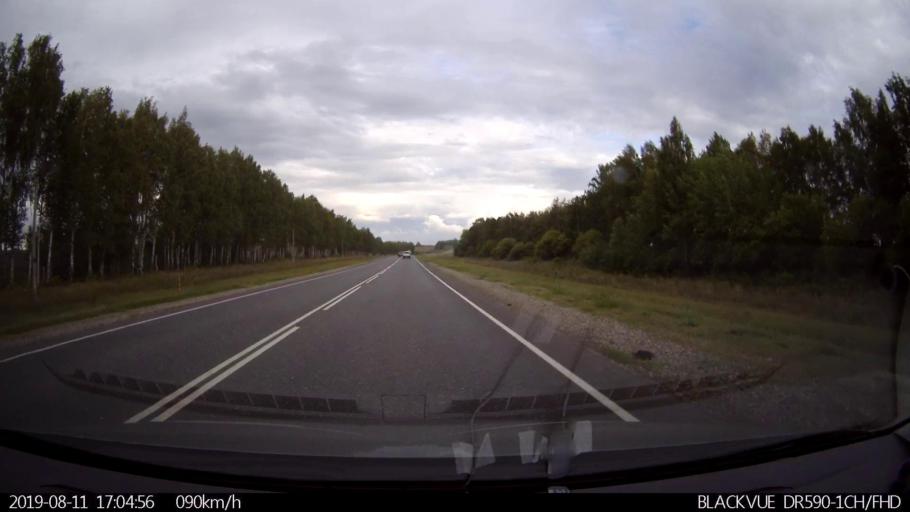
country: RU
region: Ulyanovsk
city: Mayna
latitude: 54.2997
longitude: 47.7746
